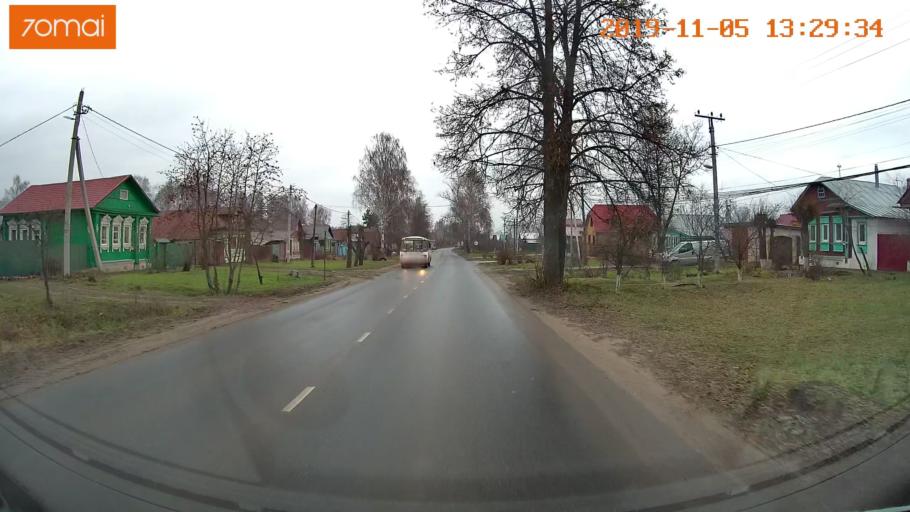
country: RU
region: Ivanovo
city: Shuya
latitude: 56.8615
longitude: 41.3975
